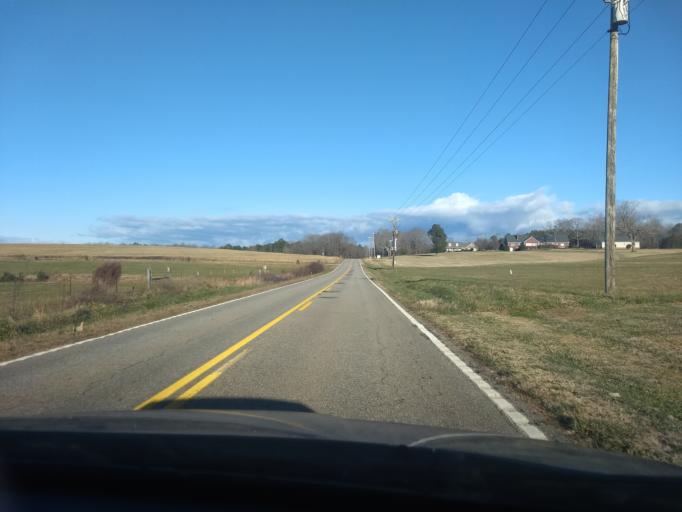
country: US
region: South Carolina
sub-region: Greenville County
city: Greer
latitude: 34.9981
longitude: -82.2099
